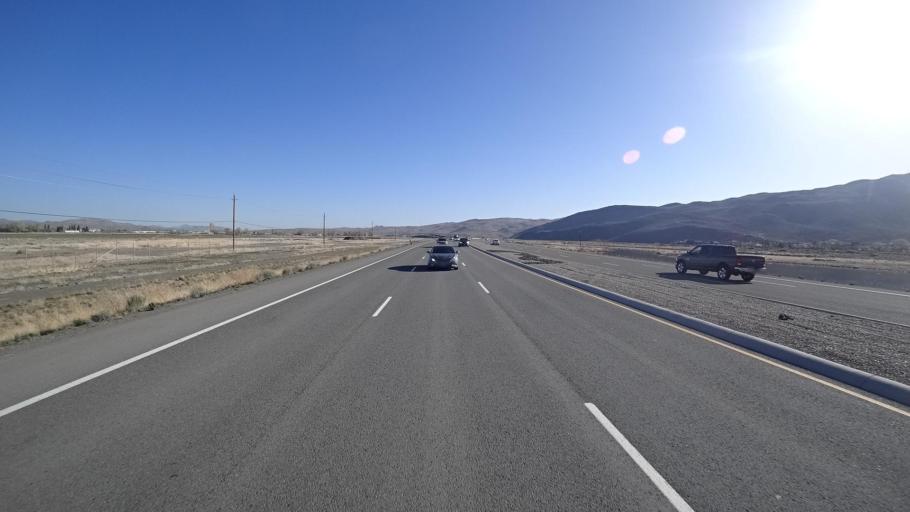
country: US
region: Nevada
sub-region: Washoe County
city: Sparks
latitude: 39.5015
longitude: -119.7269
